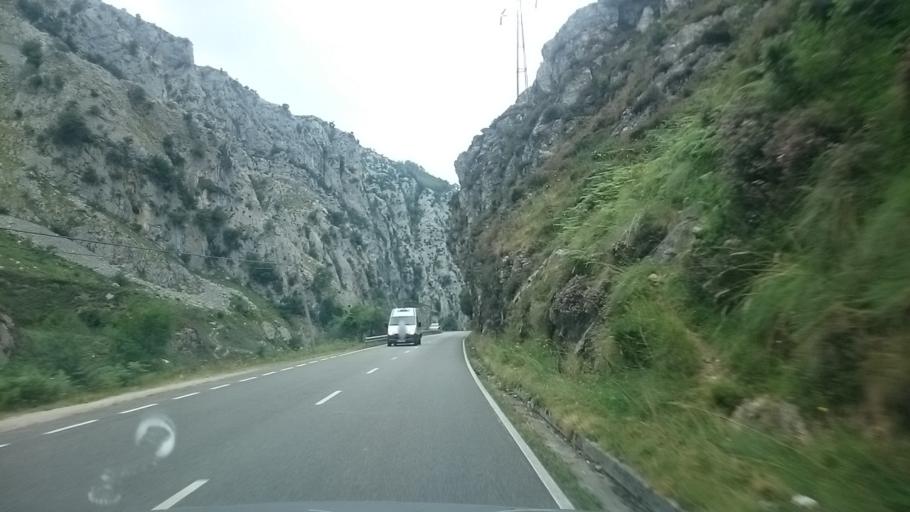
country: ES
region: Asturias
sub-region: Province of Asturias
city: Carrena
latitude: 43.2801
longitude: -4.8342
